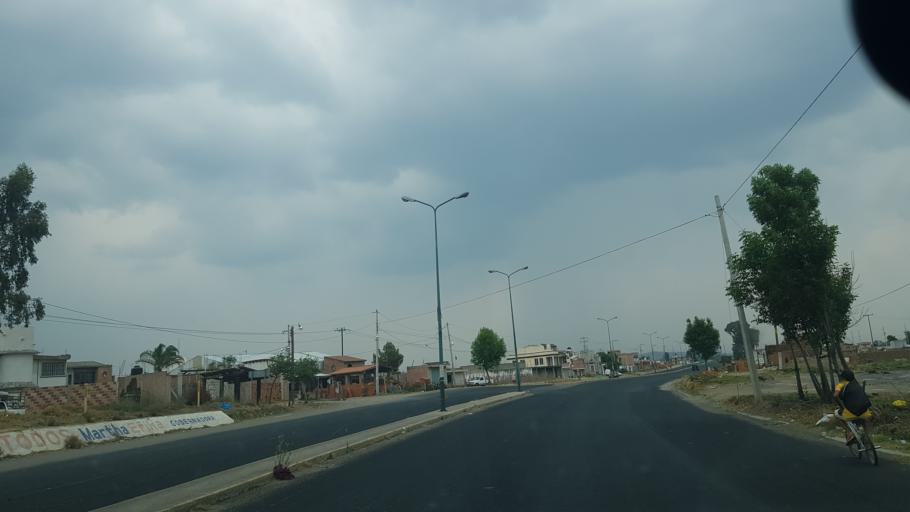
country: MX
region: Puebla
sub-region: Huejotzingo
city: San Mateo Capultitlan
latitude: 19.1779
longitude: -98.4156
